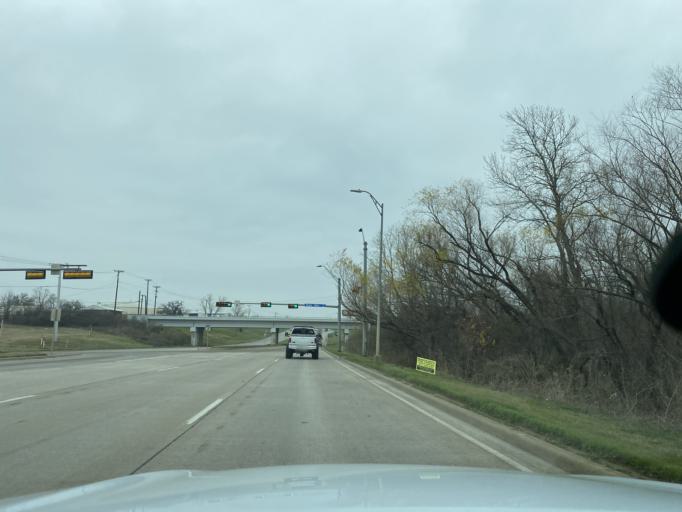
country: US
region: Texas
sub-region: Tarrant County
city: Euless
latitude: 32.8072
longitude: -97.0995
